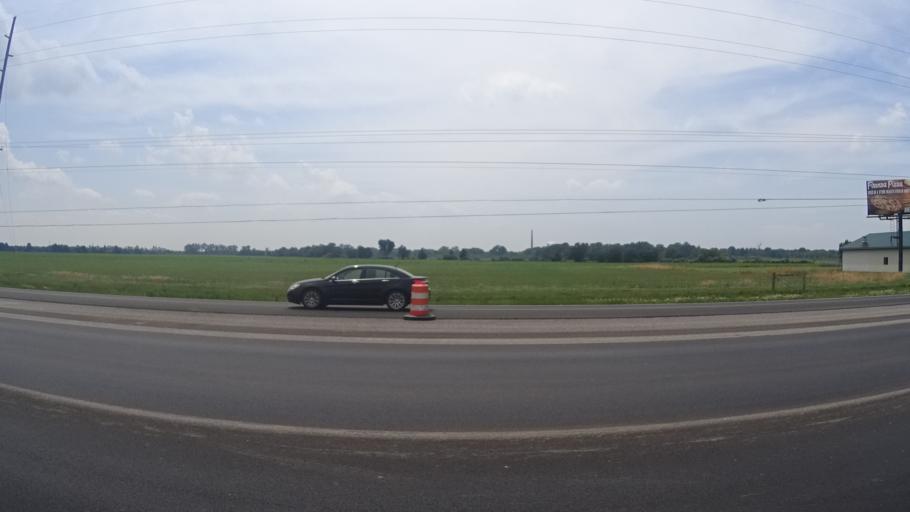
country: US
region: Ohio
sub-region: Erie County
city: Milan
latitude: 41.3515
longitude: -82.6325
